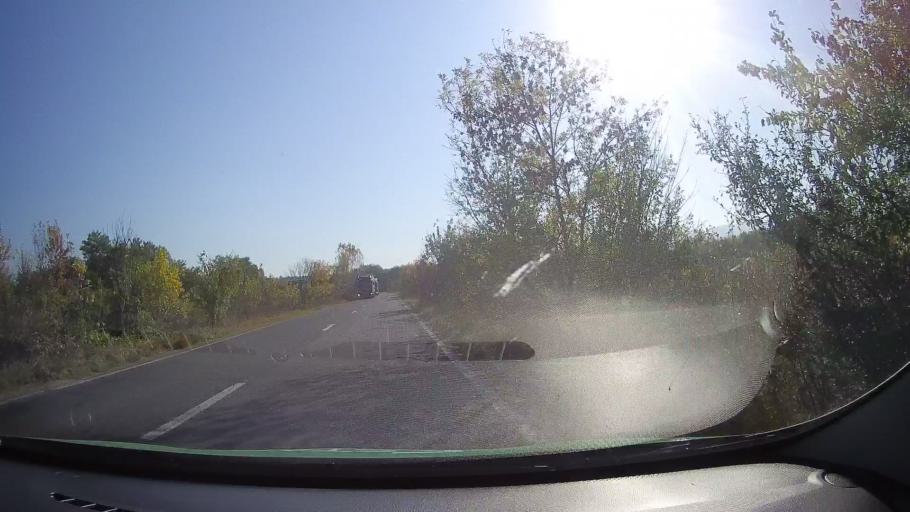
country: RO
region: Timis
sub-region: Comuna Curtea
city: Curtea
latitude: 45.8491
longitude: 22.3033
